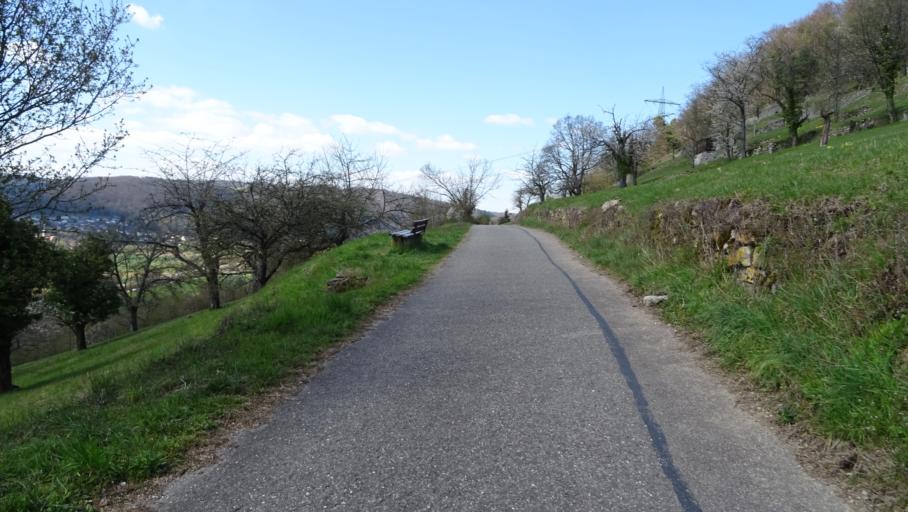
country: DE
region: Baden-Wuerttemberg
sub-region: Karlsruhe Region
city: Neckarzimmern
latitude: 49.3242
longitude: 9.1234
